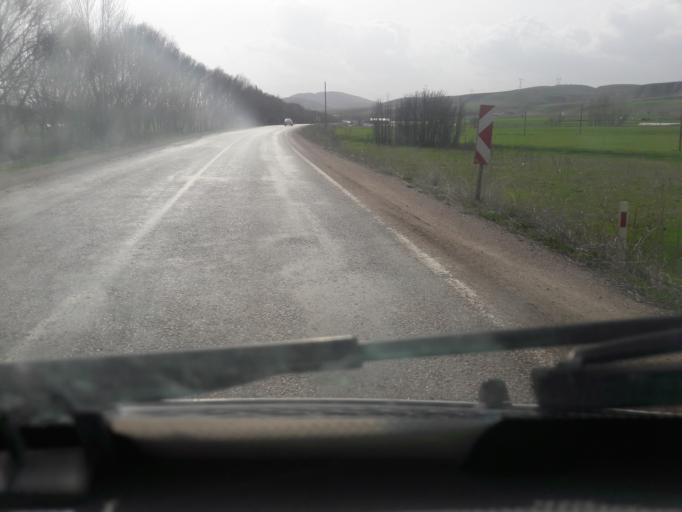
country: TR
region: Gumushane
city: Kelkit
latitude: 40.1427
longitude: 39.4229
